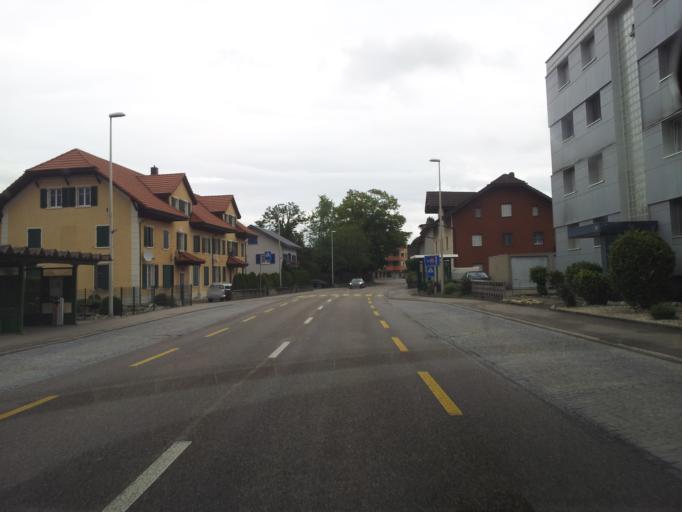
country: CH
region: Solothurn
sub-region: Bezirk Wasseramt
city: Derendingen
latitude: 47.2006
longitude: 7.5852
